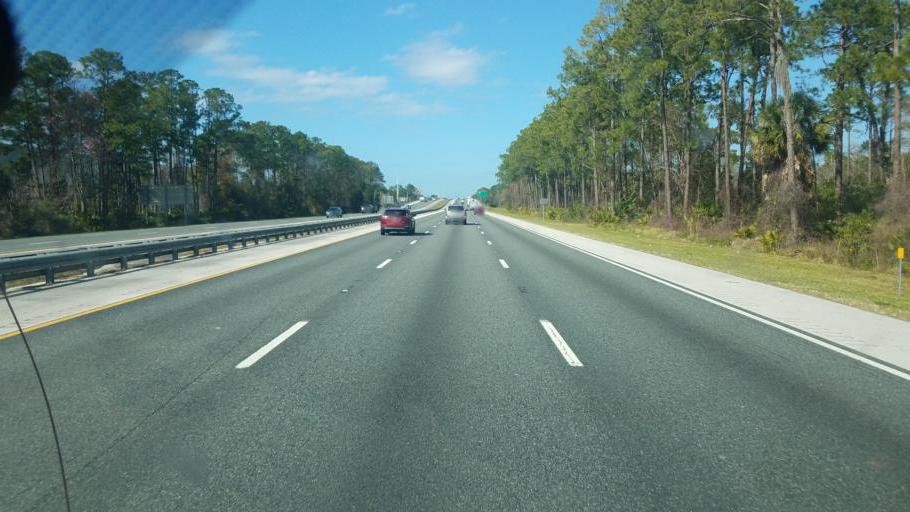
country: US
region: Florida
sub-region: Saint Johns County
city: Saint Augustine South
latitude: 29.8351
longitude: -81.3836
